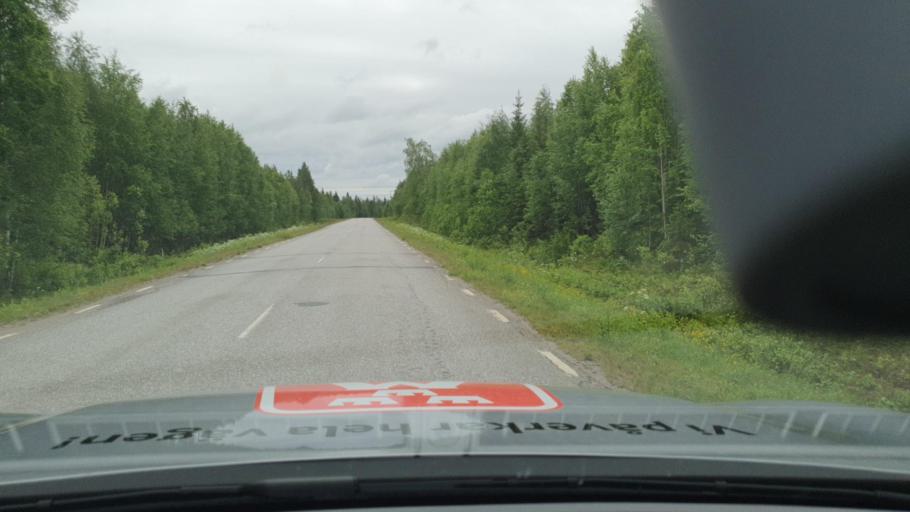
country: SE
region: Norrbotten
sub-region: Lulea Kommun
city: Ranea
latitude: 65.8677
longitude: 22.2287
